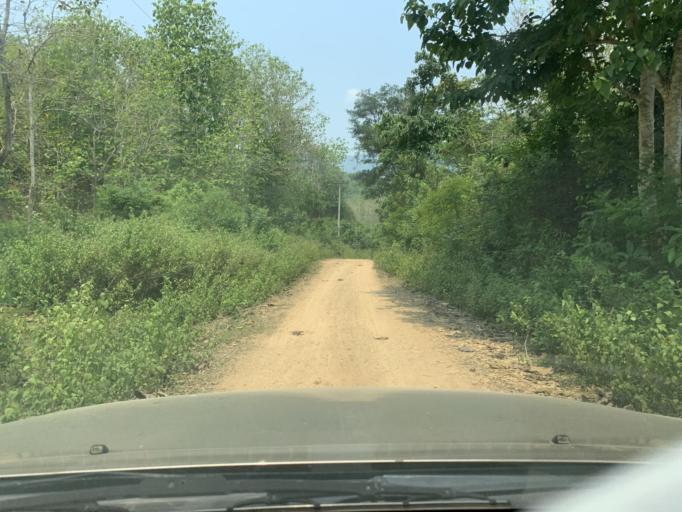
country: LA
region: Louangphabang
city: Louangphabang
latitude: 19.9619
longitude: 102.1275
